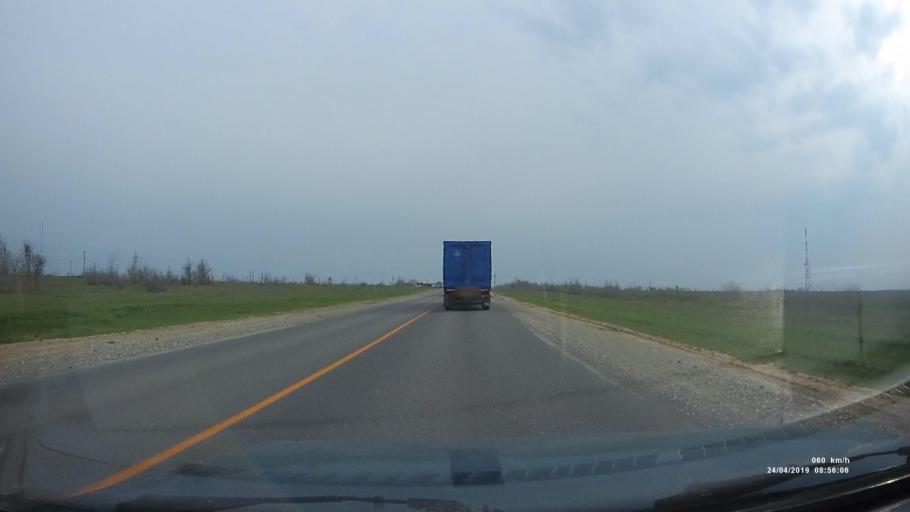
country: RU
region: Kalmykiya
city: Arshan'
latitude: 46.2995
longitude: 44.1818
